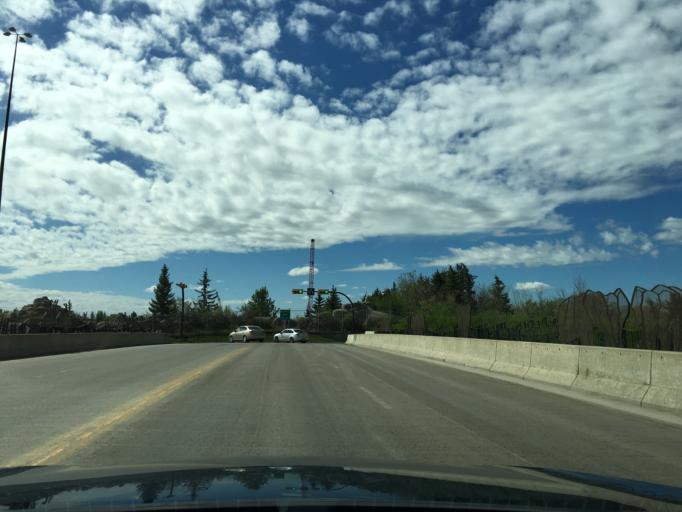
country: CA
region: Alberta
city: Calgary
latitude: 51.0481
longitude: -114.0320
